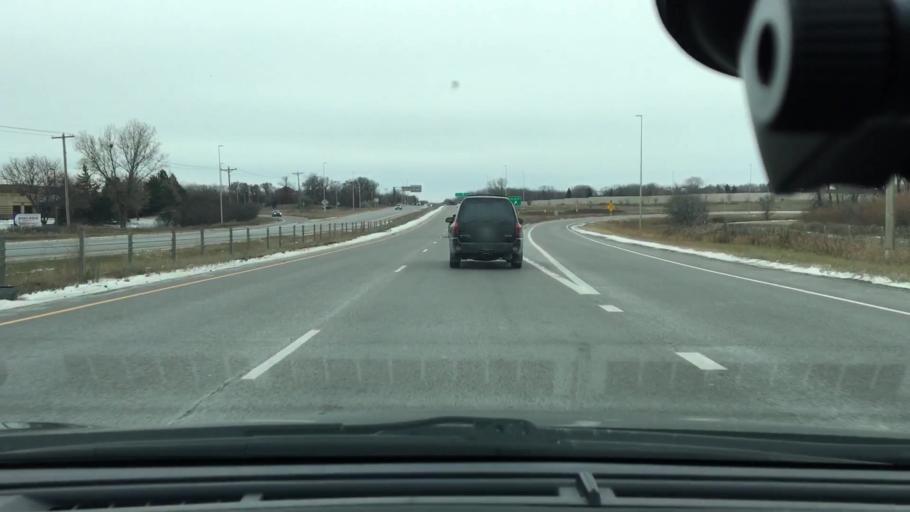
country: US
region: Minnesota
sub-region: Hennepin County
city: Osseo
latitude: 45.0872
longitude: -93.4024
